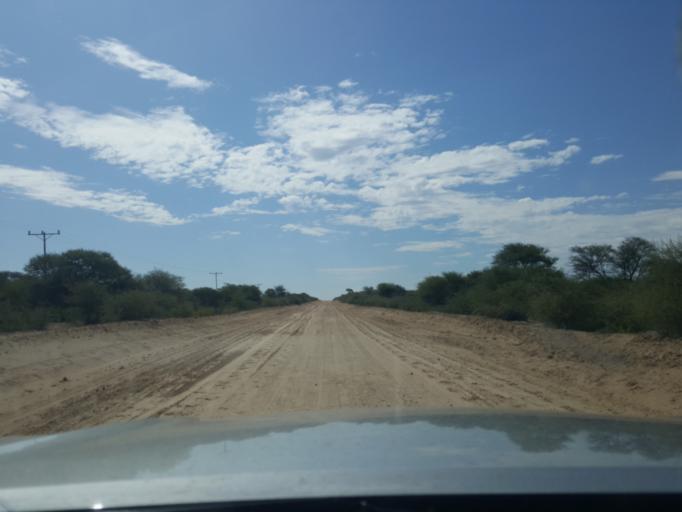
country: BW
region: Kweneng
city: Khudumelapye
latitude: -23.8769
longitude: 24.9032
